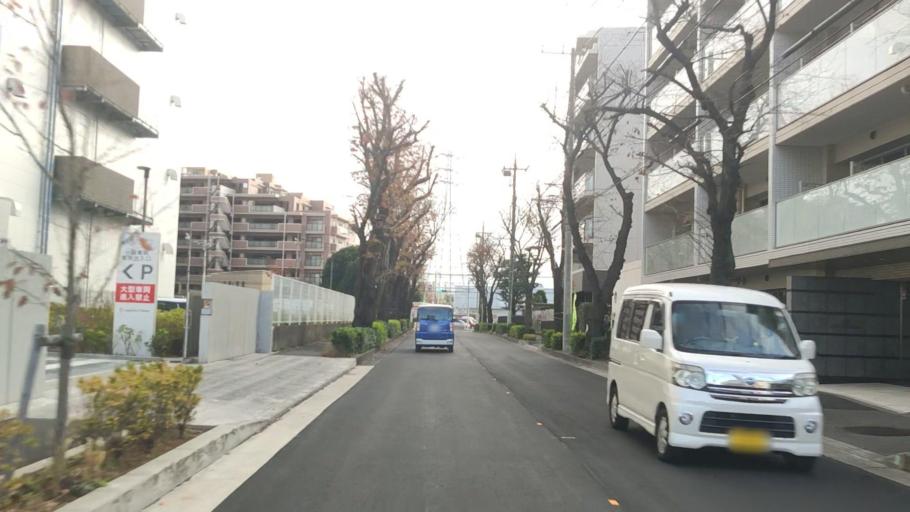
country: JP
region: Kanagawa
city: Minami-rinkan
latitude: 35.5025
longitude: 139.4519
